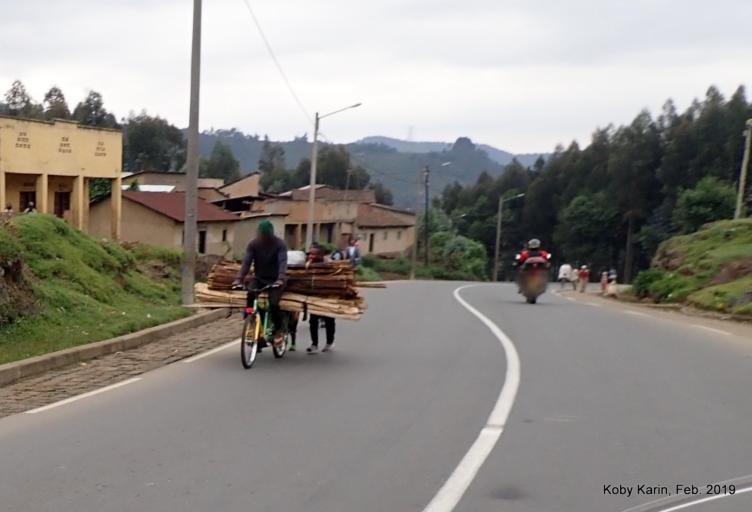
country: RW
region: Northern Province
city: Musanze
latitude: -1.6199
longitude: 29.4591
